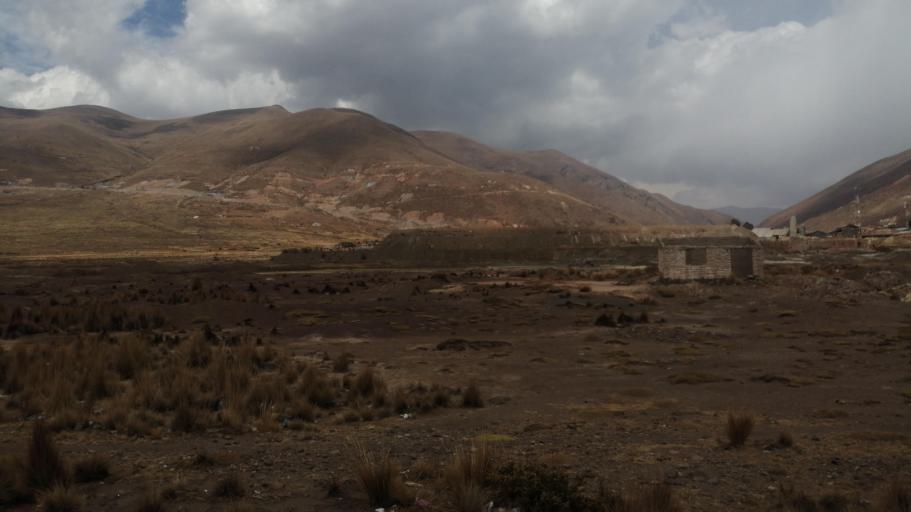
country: BO
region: Oruro
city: Poopo
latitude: -18.3805
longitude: -66.9801
